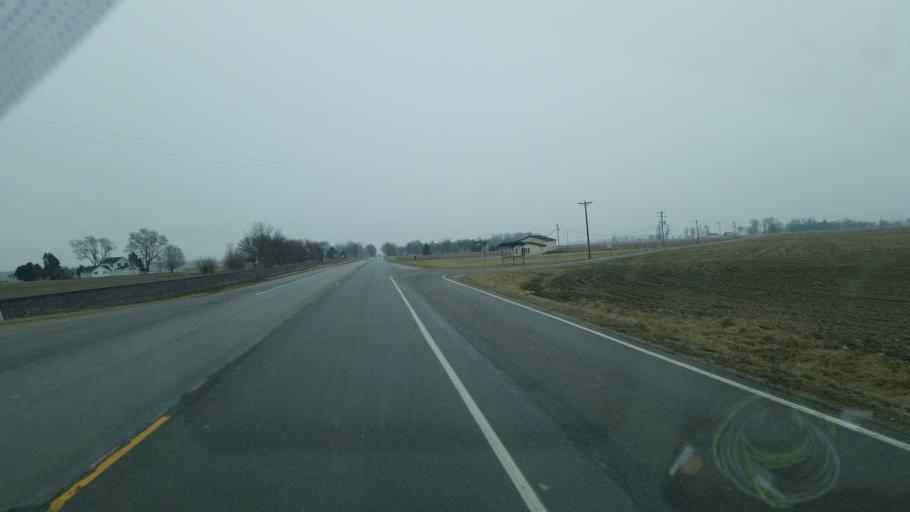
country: US
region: Indiana
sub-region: Wabash County
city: Wabash
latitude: 40.7573
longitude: -85.8101
